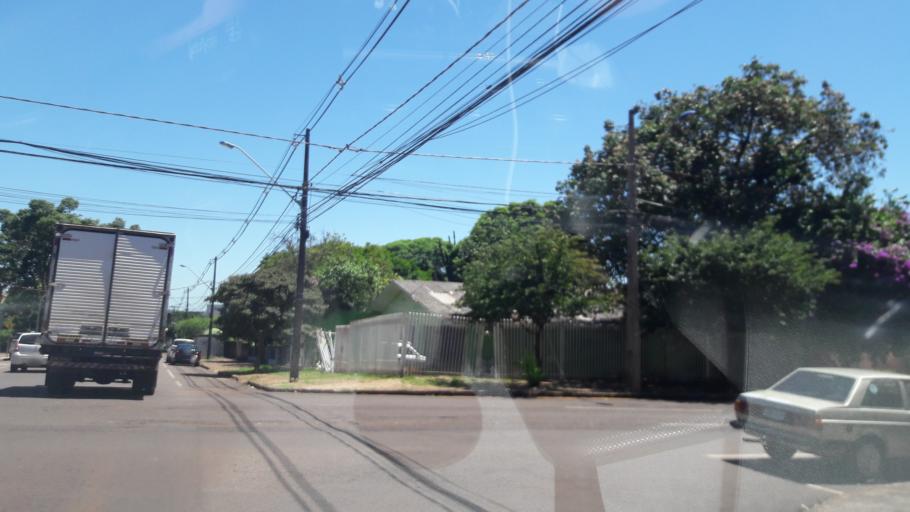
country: BR
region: Parana
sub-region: Cascavel
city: Cascavel
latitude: -24.9512
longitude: -53.4750
